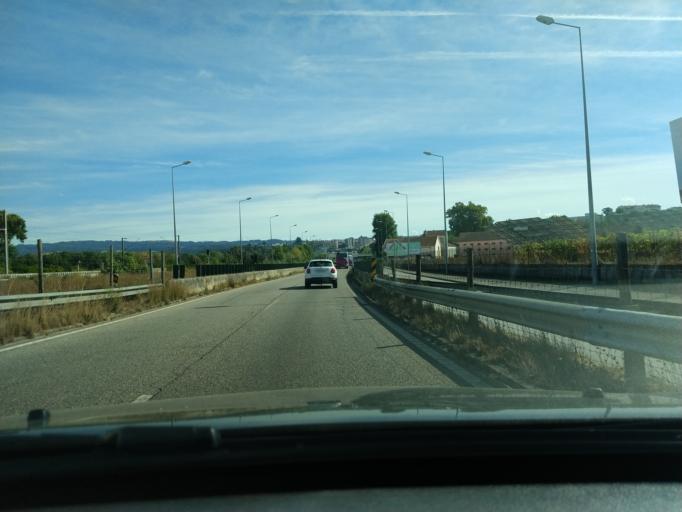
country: PT
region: Coimbra
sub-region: Coimbra
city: Coimbra
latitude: 40.2143
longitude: -8.4557
